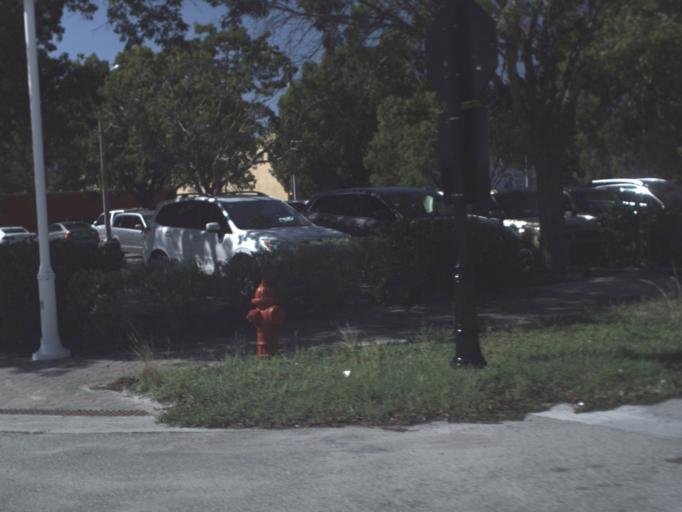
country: US
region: Florida
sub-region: Collier County
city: Naples
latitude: 26.1528
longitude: -81.7965
